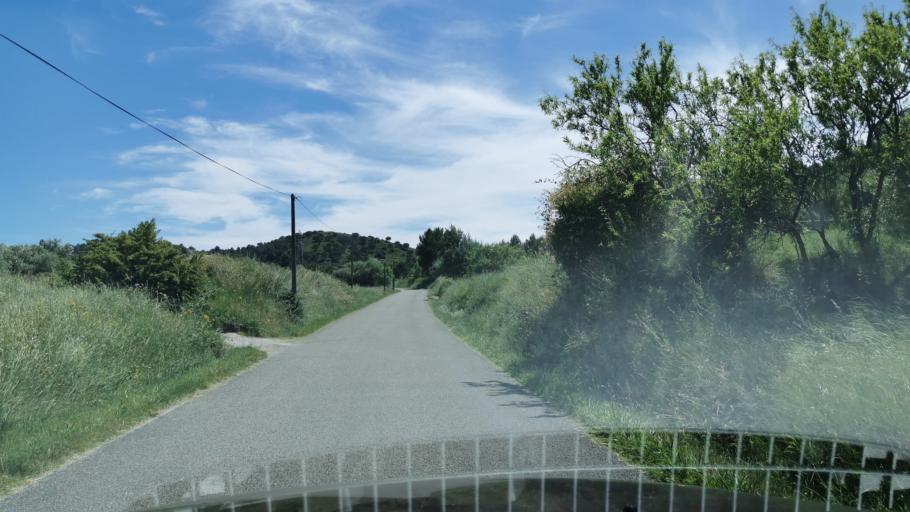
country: FR
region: Languedoc-Roussillon
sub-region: Departement de l'Aude
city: Nevian
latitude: 43.2062
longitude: 2.9033
